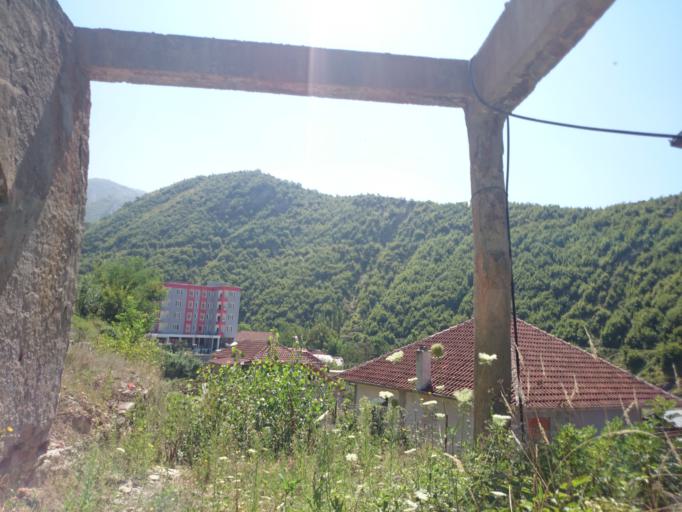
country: AL
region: Diber
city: Peshkopi
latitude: 41.6860
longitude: 20.4424
